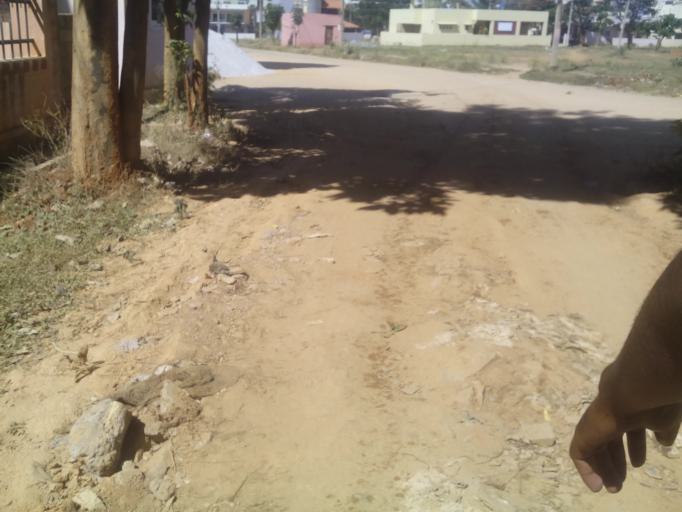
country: IN
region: Karnataka
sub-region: Bangalore Urban
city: Anekal
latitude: 12.7897
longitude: 77.7038
